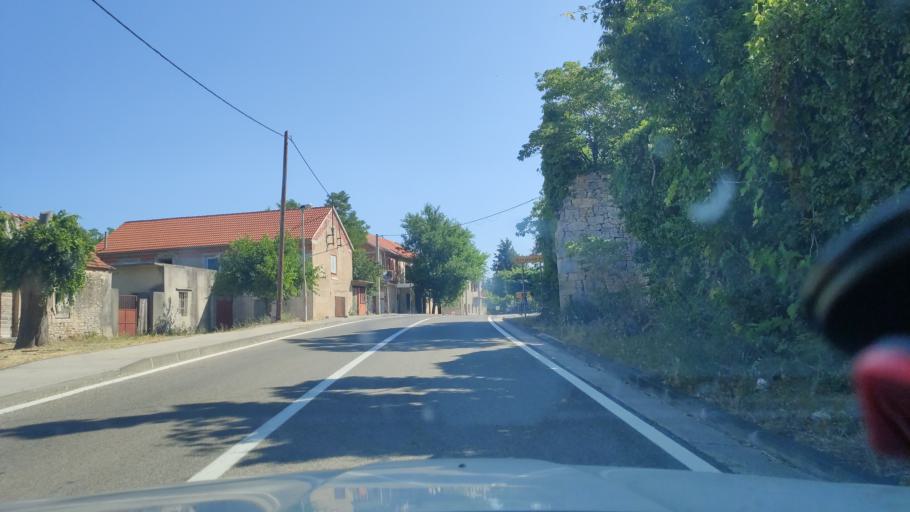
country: HR
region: Sibensko-Kniniska
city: Kistanje
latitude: 43.9524
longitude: 15.8504
